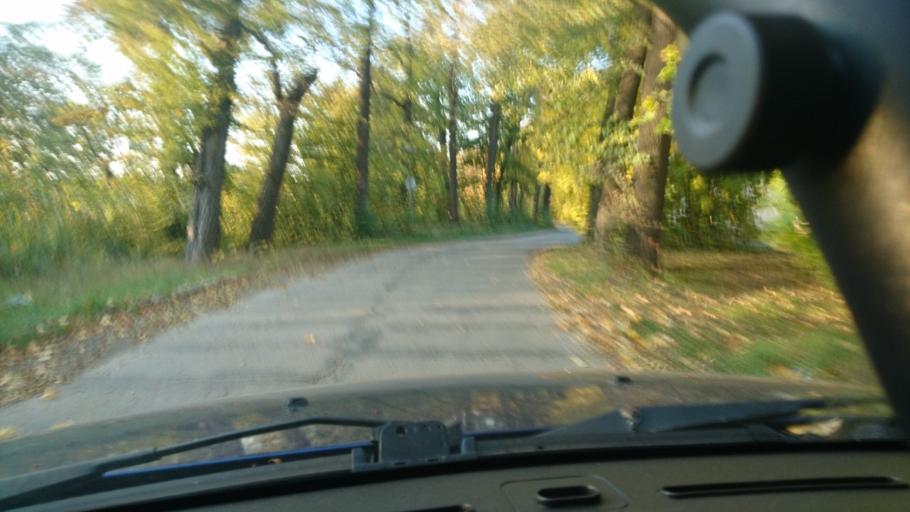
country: PL
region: Silesian Voivodeship
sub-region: Powiat bielski
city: Mazancowice
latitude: 49.8265
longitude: 18.9794
